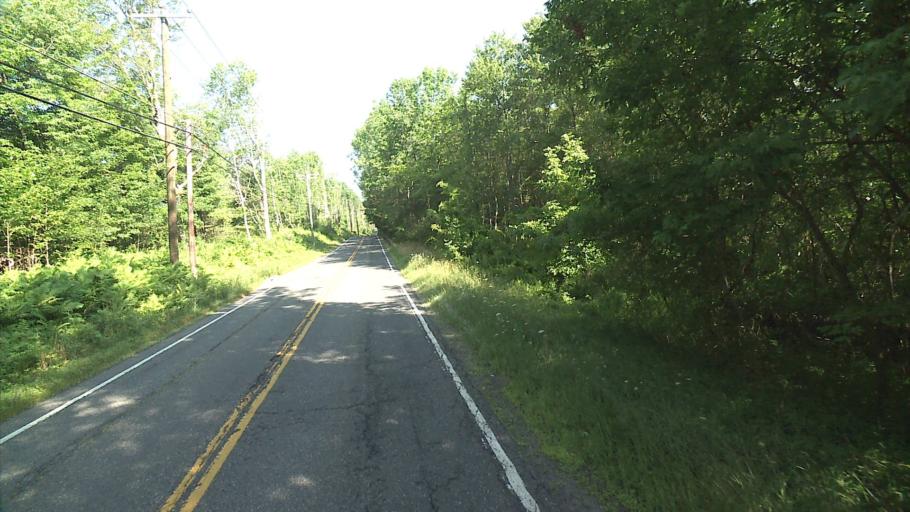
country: US
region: Connecticut
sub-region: Litchfield County
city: Winsted
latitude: 41.9989
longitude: -73.1018
